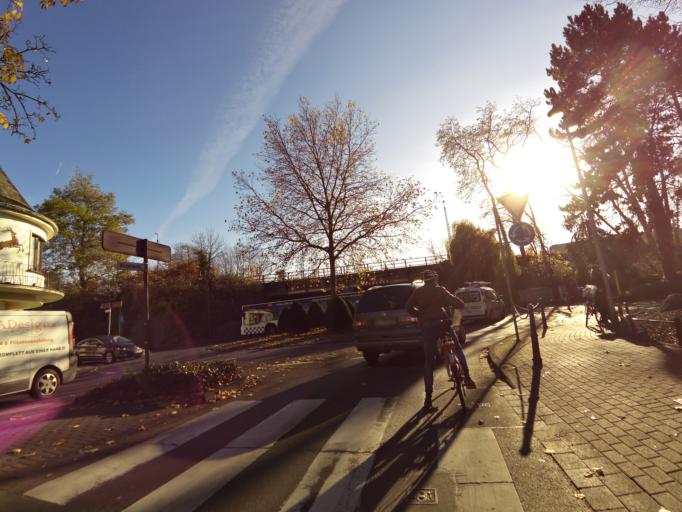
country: DE
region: North Rhine-Westphalia
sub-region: Regierungsbezirk Koln
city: Euskirchen
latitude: 50.6572
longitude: 6.7873
